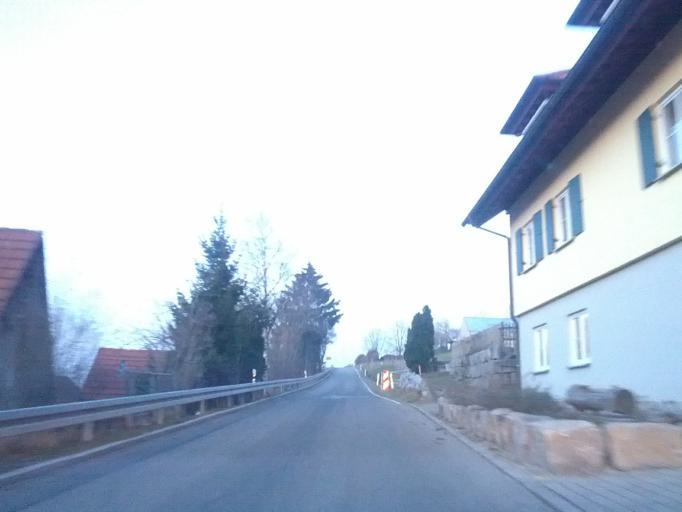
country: DE
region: Baden-Wuerttemberg
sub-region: Tuebingen Region
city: Steinhausen an der Rottum
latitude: 47.9540
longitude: 9.9880
